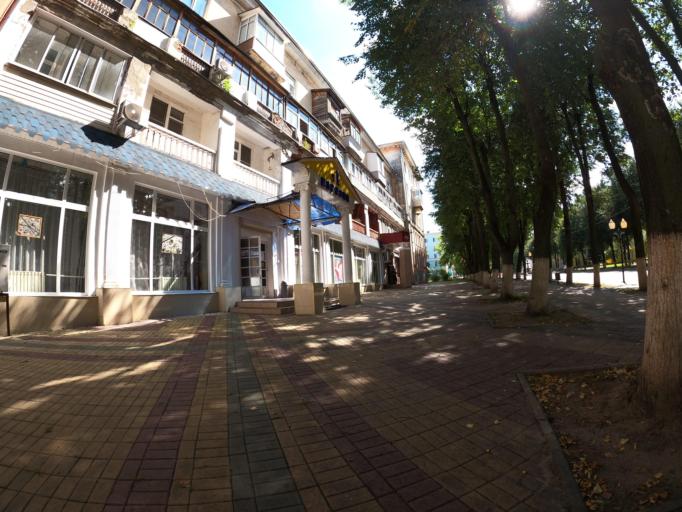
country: RU
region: Moskovskaya
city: Stupino
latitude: 54.8891
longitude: 38.0790
